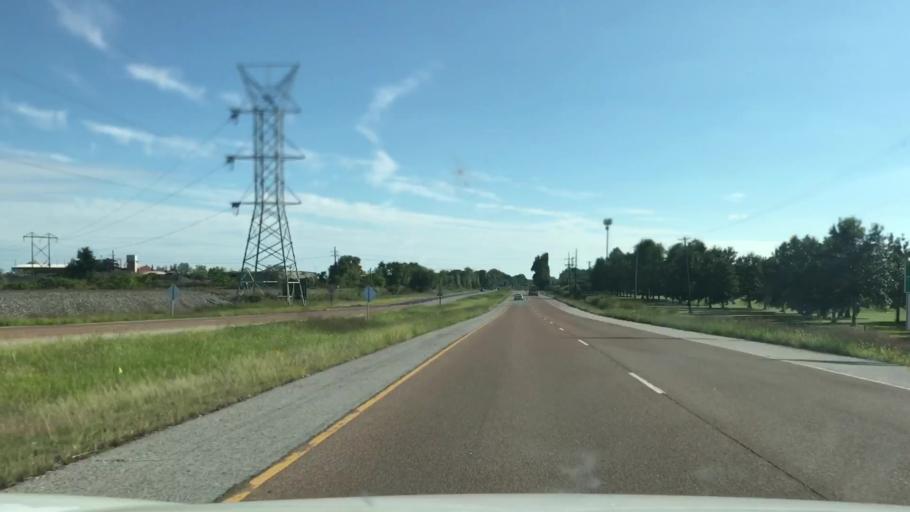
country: US
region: Illinois
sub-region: Madison County
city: Hartford
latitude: 38.8027
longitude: -90.1003
